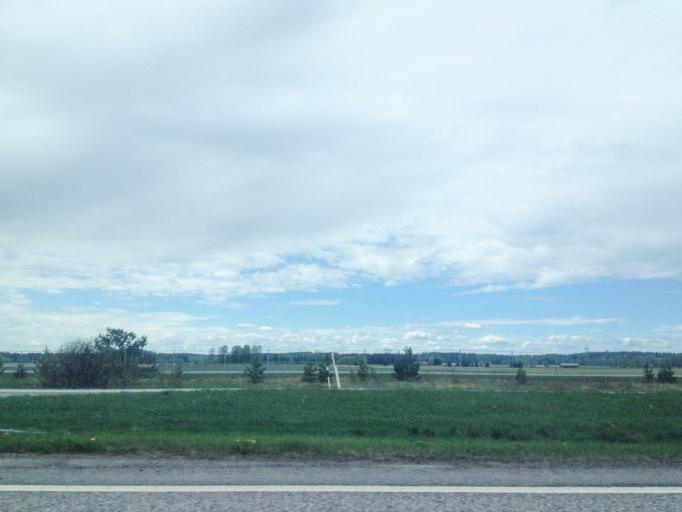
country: FI
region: Uusimaa
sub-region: Helsinki
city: Nurmijaervi
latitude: 60.5245
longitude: 24.8444
